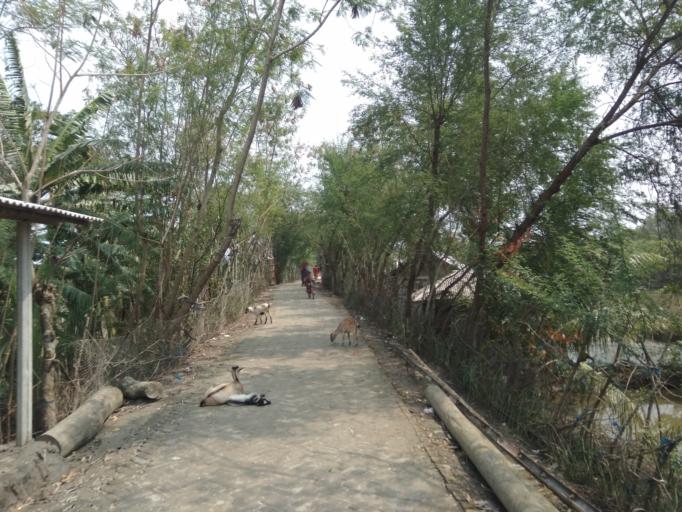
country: IN
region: West Bengal
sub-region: North 24 Parganas
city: Taki
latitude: 22.2812
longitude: 89.2933
